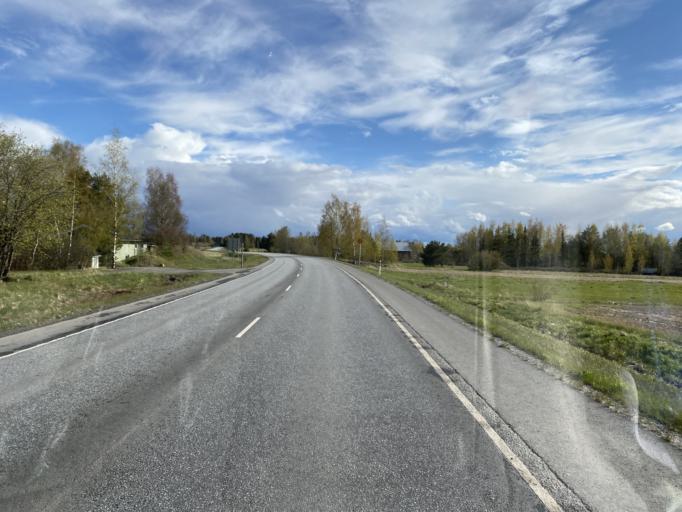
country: FI
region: Pirkanmaa
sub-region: Tampere
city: Lempaeaelae
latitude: 61.2933
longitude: 23.7423
